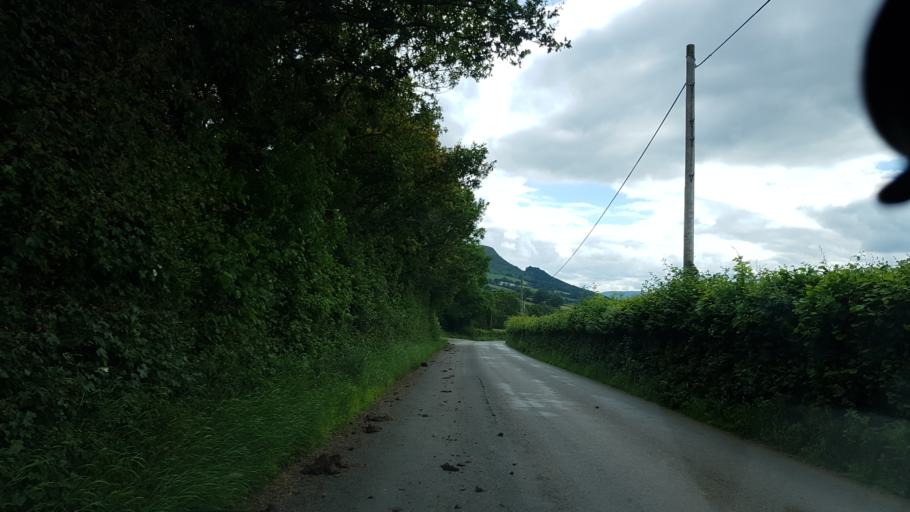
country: GB
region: England
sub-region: Herefordshire
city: Llancillo
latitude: 51.8848
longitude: -2.9527
